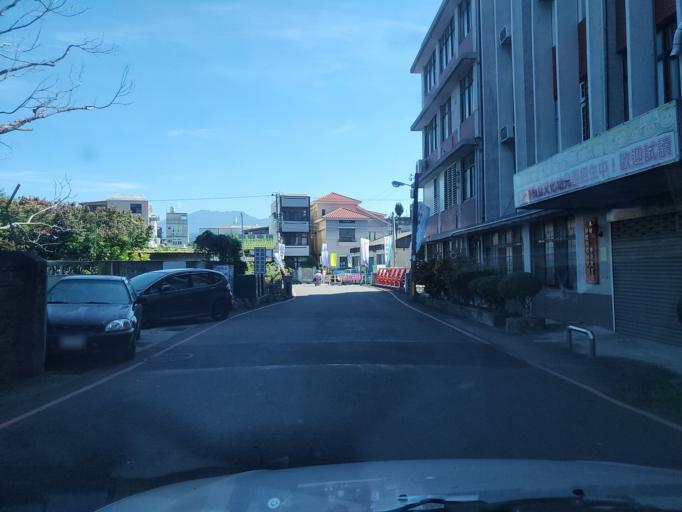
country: TW
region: Taiwan
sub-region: Miaoli
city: Miaoli
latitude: 24.5605
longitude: 120.8238
